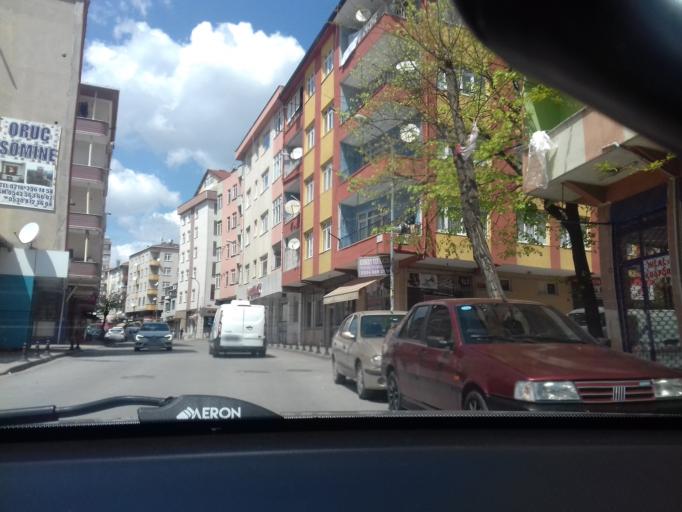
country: TR
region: Istanbul
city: Pendik
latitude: 40.8713
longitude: 29.2721
